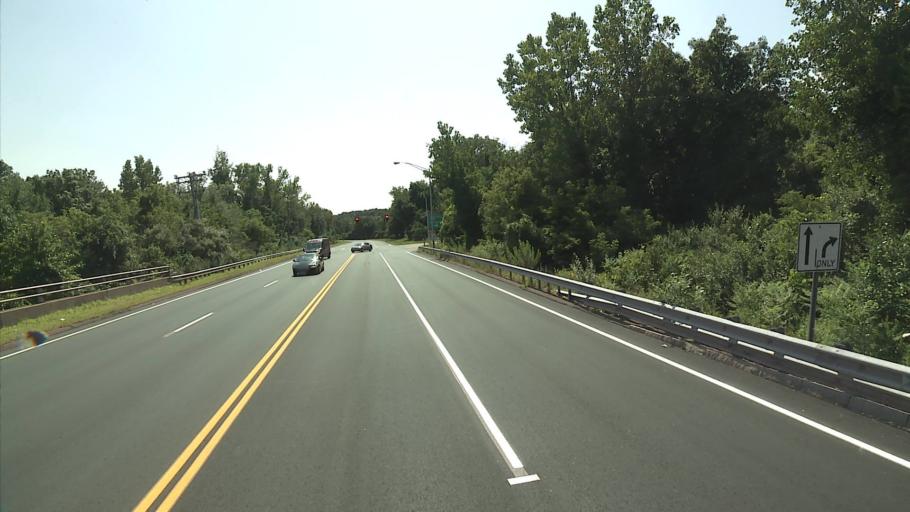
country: US
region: Connecticut
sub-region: Hartford County
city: Windsor Locks
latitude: 41.9109
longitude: -72.6289
